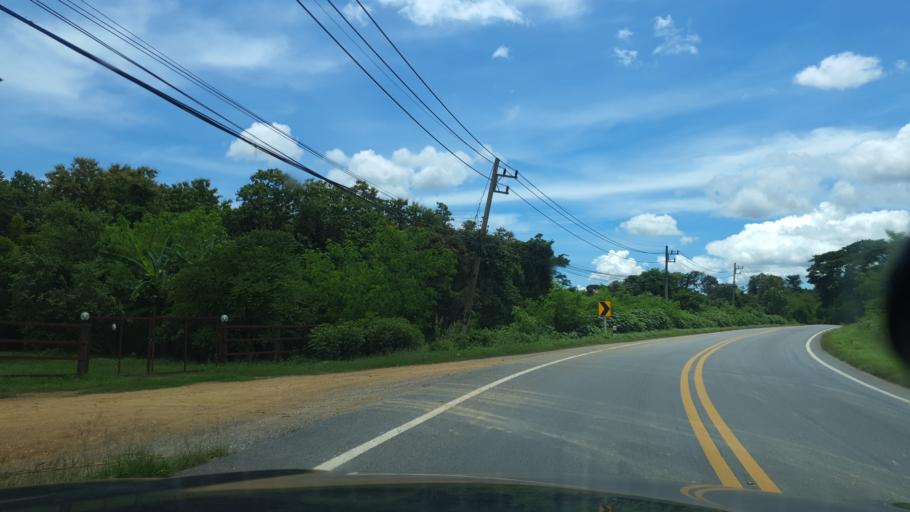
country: TH
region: Sukhothai
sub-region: Amphoe Si Satchanalai
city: Si Satchanalai
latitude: 17.6285
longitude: 99.7009
